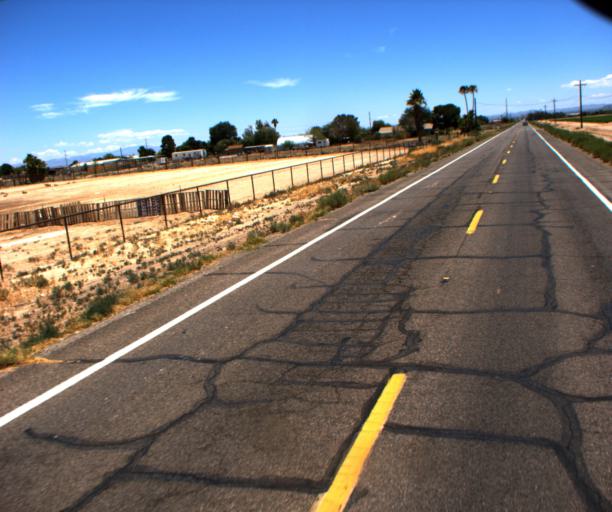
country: US
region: Arizona
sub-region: Pinal County
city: Coolidge
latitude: 32.8795
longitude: -111.5233
